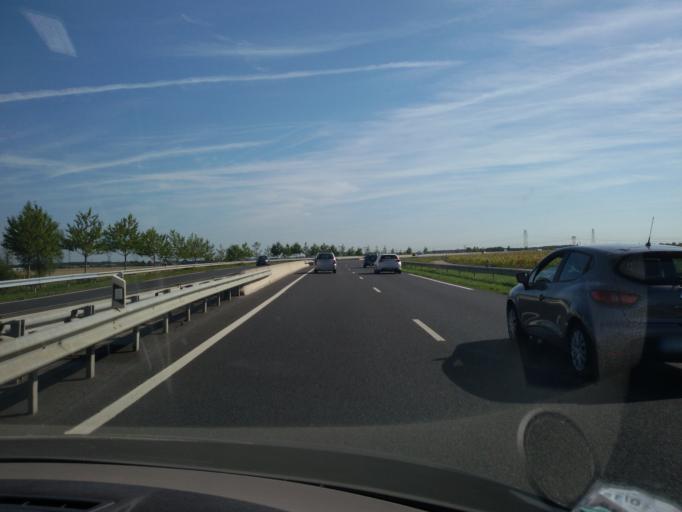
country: FR
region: Ile-de-France
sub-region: Departement de l'Essonne
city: La Norville
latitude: 48.5752
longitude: 2.2632
